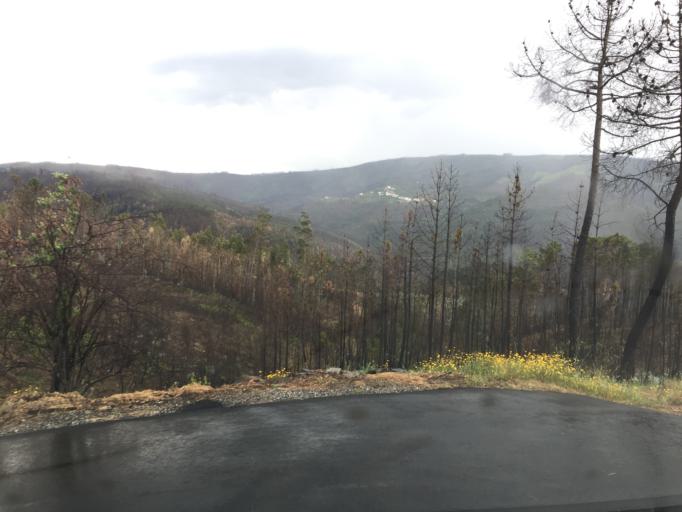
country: PT
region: Coimbra
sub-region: Pampilhosa da Serra
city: Pampilhosa da Serra
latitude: 40.0352
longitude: -8.0036
